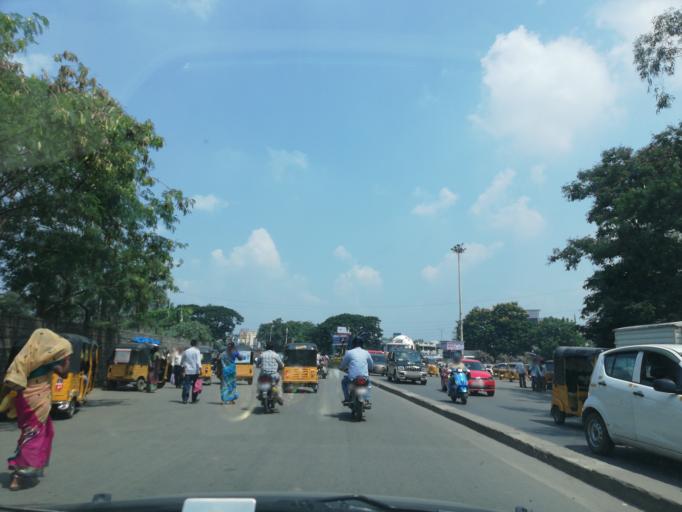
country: IN
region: Telangana
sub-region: Medak
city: Serilingampalle
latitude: 17.4941
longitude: 78.3159
